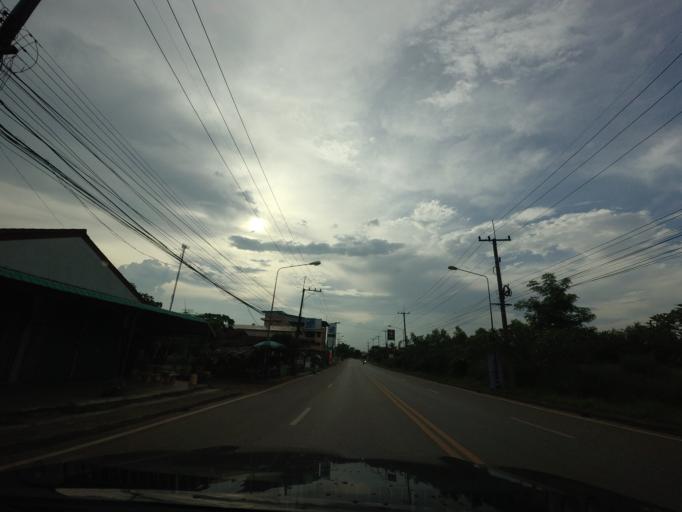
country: TH
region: Changwat Udon Thani
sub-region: Amphoe Ban Phue
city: Ban Phue
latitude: 17.6956
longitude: 102.4571
